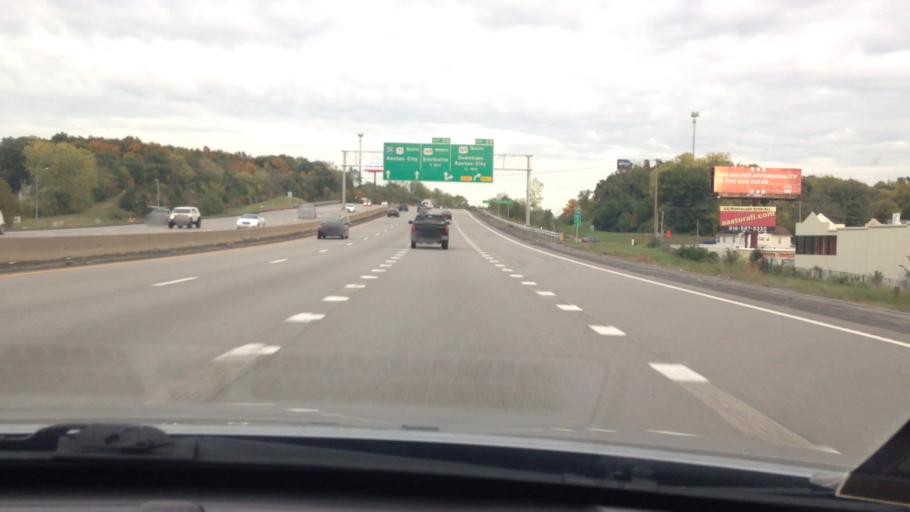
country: US
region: Missouri
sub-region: Platte County
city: Riverside
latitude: 39.1886
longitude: -94.6086
